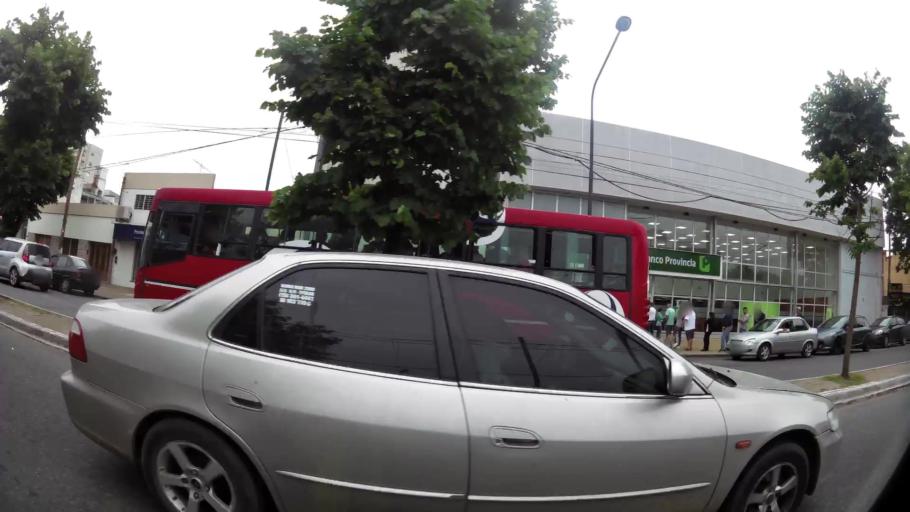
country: AR
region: Buenos Aires
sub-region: Partido de La Plata
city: La Plata
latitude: -34.9300
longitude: -57.9764
